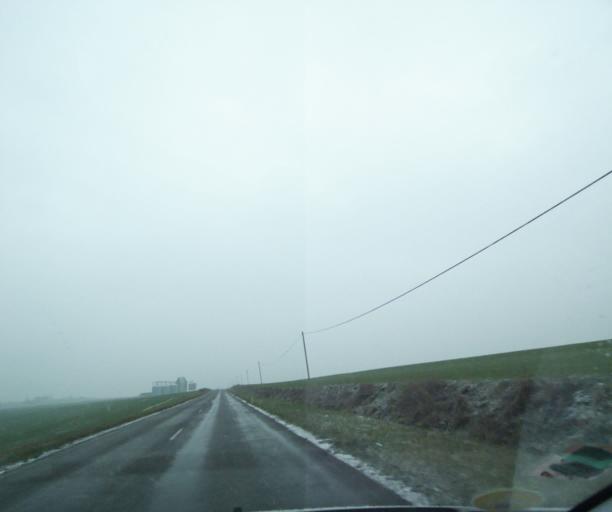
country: FR
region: Champagne-Ardenne
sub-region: Departement de la Haute-Marne
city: Wassy
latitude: 48.4870
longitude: 4.9792
